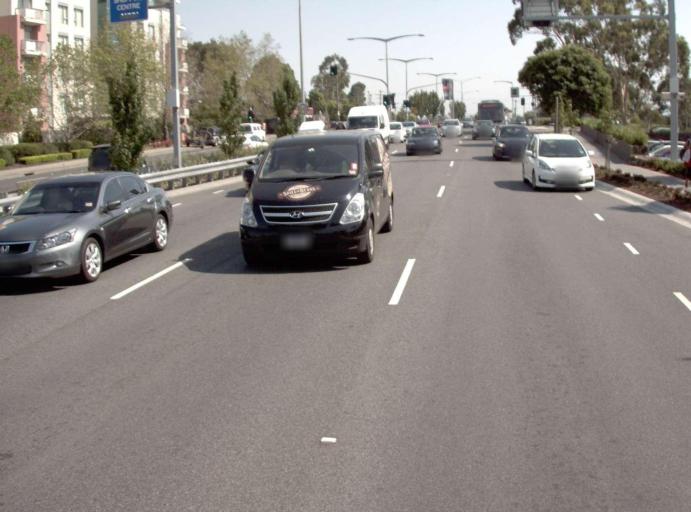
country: AU
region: Victoria
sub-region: Manningham
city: Doncaster
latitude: -37.7843
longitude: 145.1244
